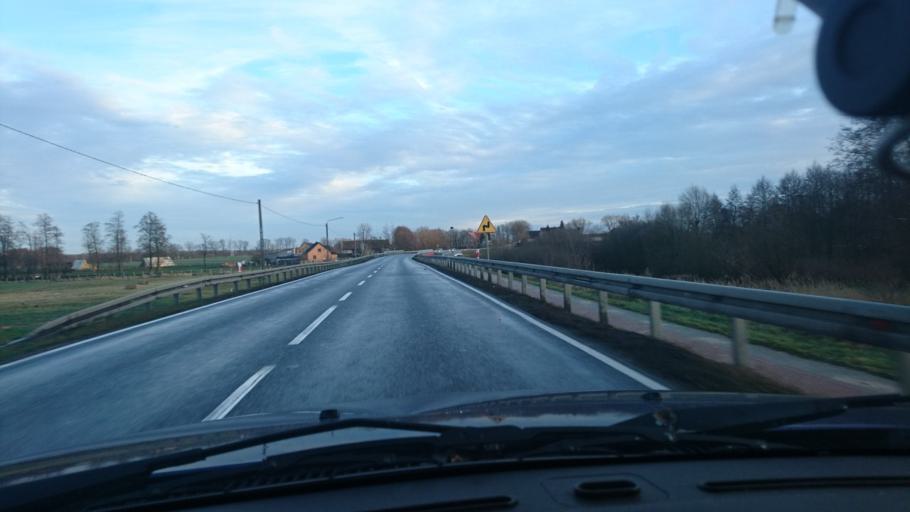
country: PL
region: Greater Poland Voivodeship
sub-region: Powiat kepinski
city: Opatow
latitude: 51.1650
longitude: 18.1494
